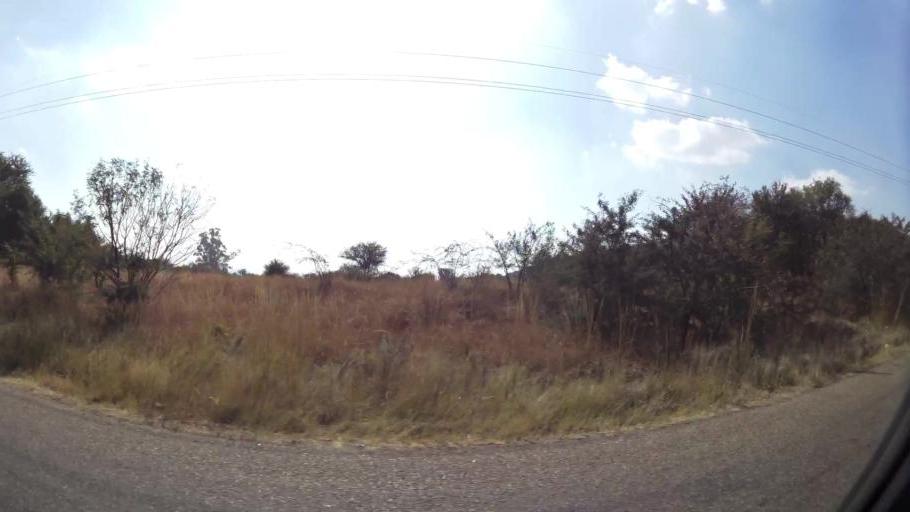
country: ZA
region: North-West
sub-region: Bojanala Platinum District Municipality
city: Rustenburg
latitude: -25.6328
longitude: 27.1731
